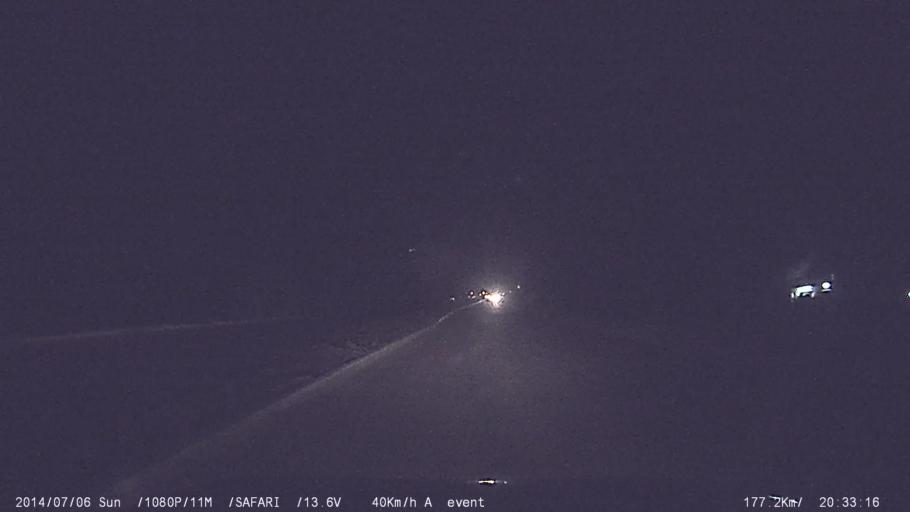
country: IN
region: Kerala
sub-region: Palakkad district
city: Chittur
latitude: 10.8065
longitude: 76.7899
